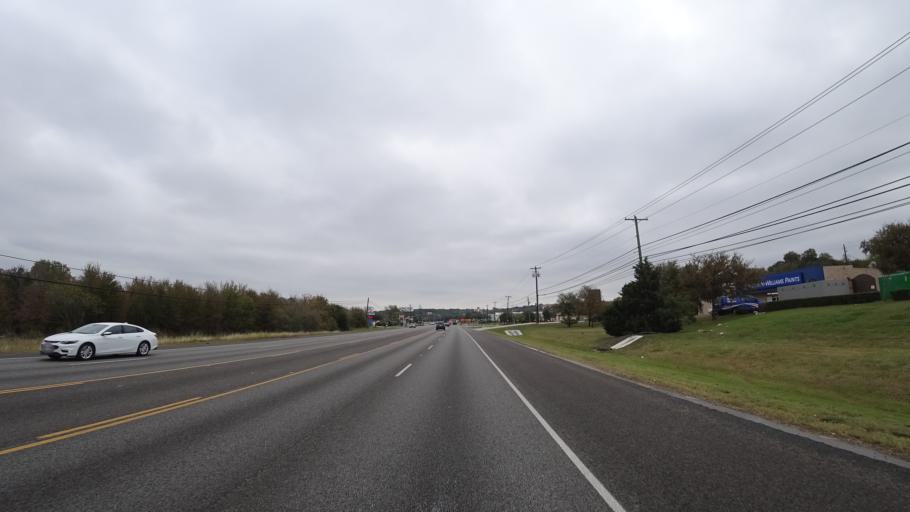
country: US
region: Texas
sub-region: Travis County
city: Barton Creek
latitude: 30.2383
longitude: -97.8793
